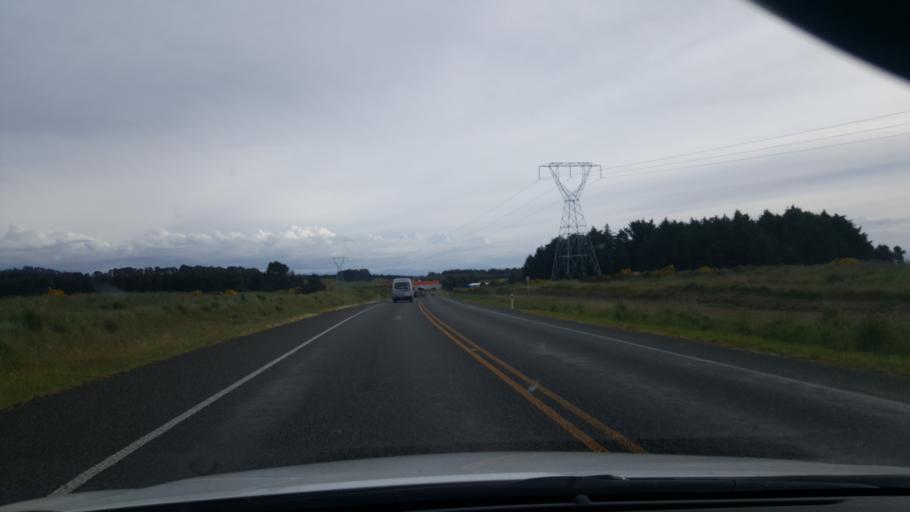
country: NZ
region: Waikato
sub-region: Taupo District
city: Taupo
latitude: -38.6952
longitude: 176.1136
